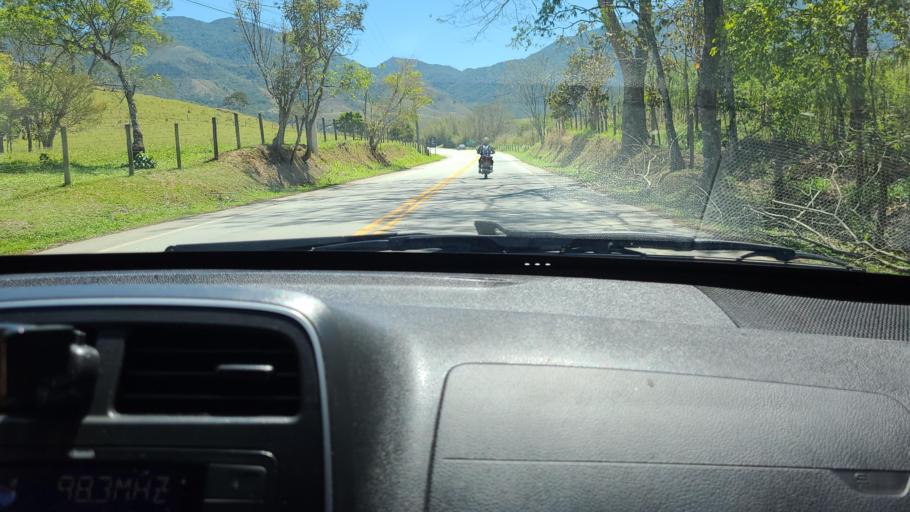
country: BR
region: Sao Paulo
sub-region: Tremembe
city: Tremembe
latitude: -22.8609
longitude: -45.5893
